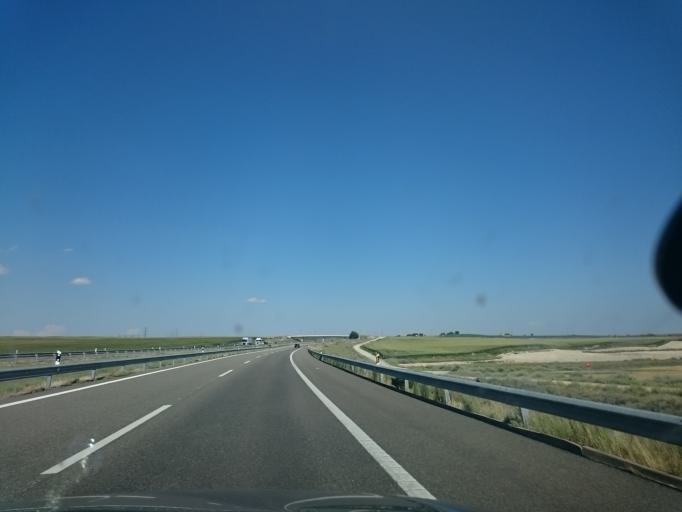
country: ES
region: Aragon
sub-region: Provincia de Huesca
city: Valfarta
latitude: 41.5193
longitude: -0.1173
